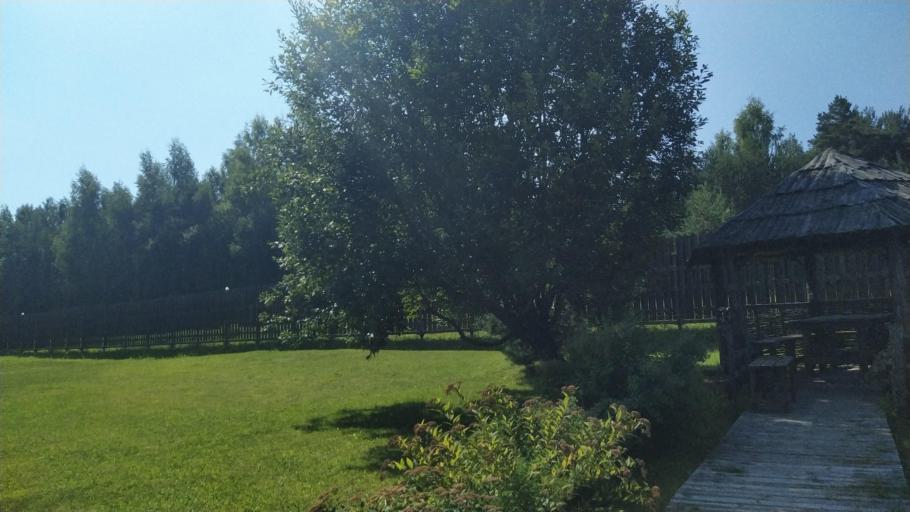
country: RU
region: Pskov
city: Pushkinskiye Gory
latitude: 56.9825
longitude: 29.0031
